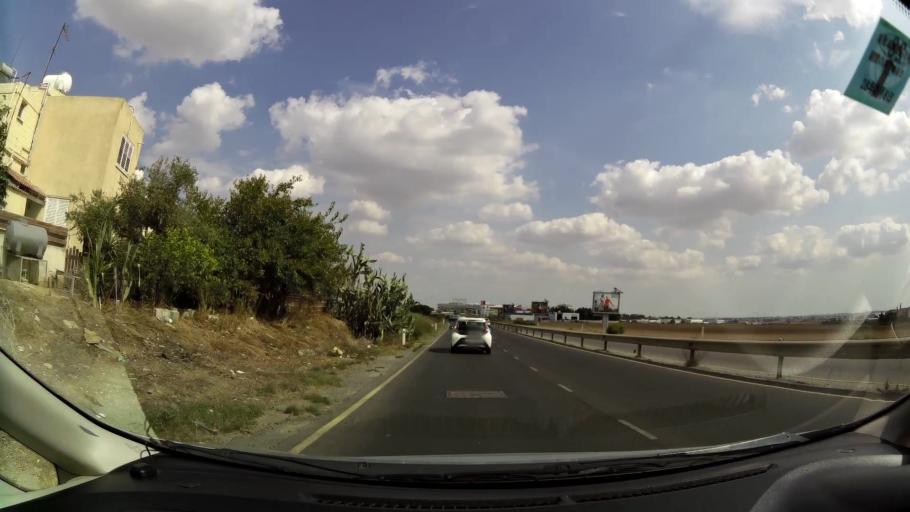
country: CY
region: Lefkosia
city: Nicosia
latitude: 35.1245
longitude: 33.3481
